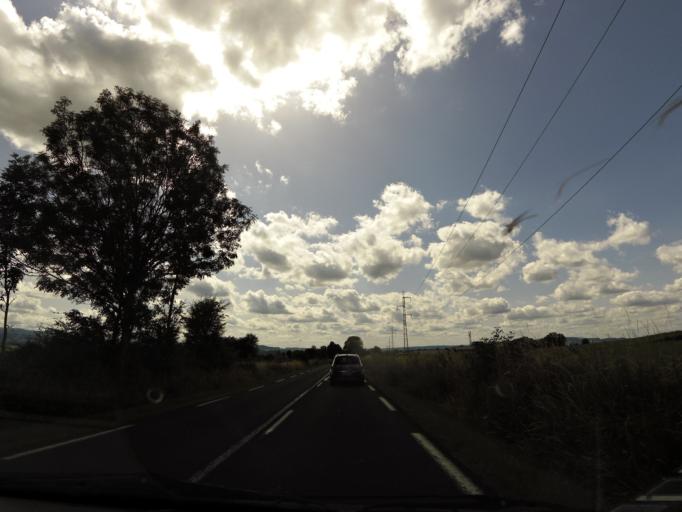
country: FR
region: Auvergne
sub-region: Departement du Puy-de-Dome
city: Aydat
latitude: 45.7309
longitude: 2.9098
